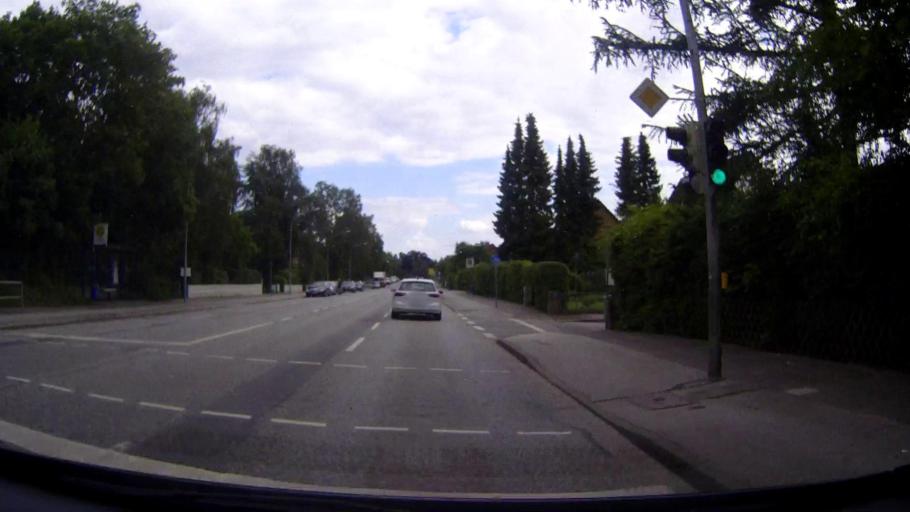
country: DE
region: Schleswig-Holstein
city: Stockelsdorf
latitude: 53.8530
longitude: 10.6402
